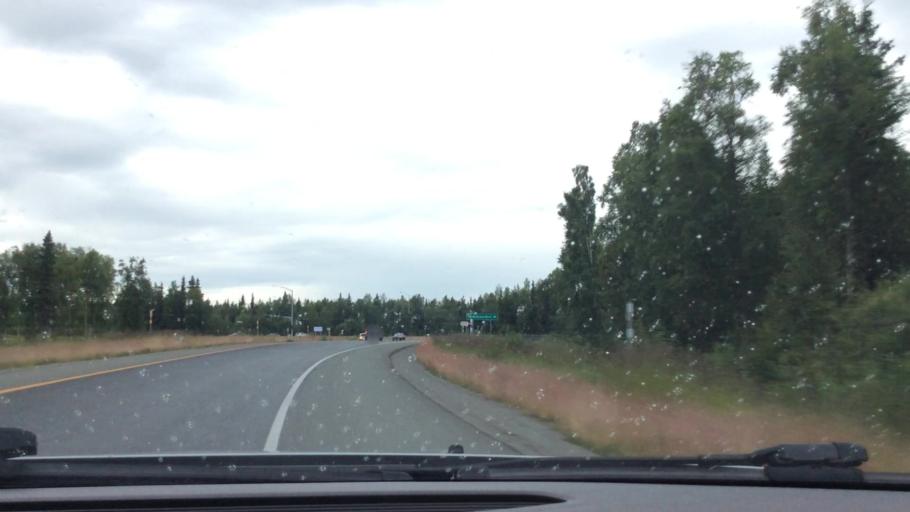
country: US
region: Alaska
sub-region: Anchorage Municipality
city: Anchorage
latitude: 61.2252
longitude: -149.7737
